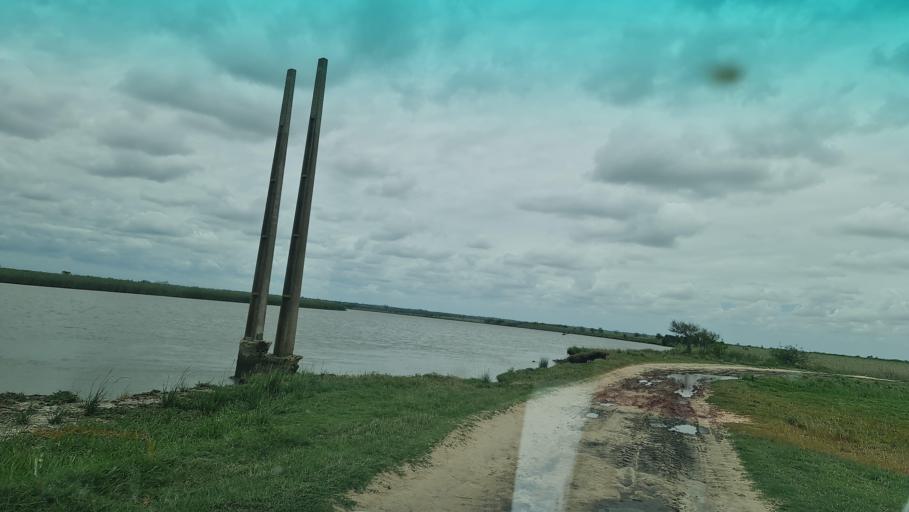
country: MZ
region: Maputo City
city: Maputo
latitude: -25.7221
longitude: 32.6992
